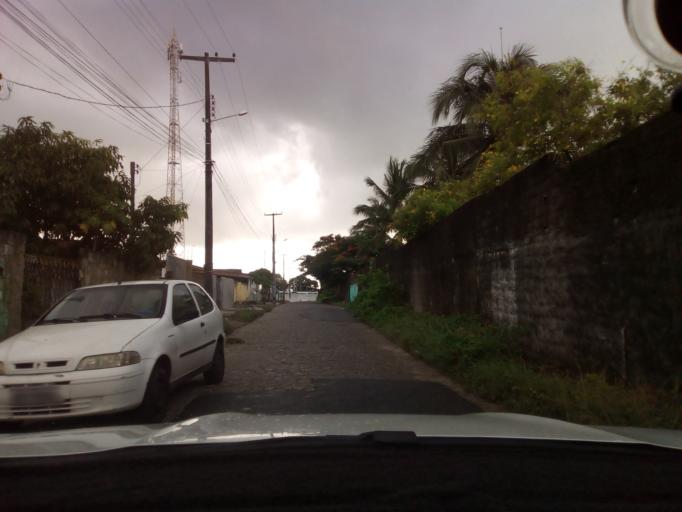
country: BR
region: Paraiba
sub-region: Bayeux
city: Bayeux
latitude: -7.1695
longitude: -34.8950
